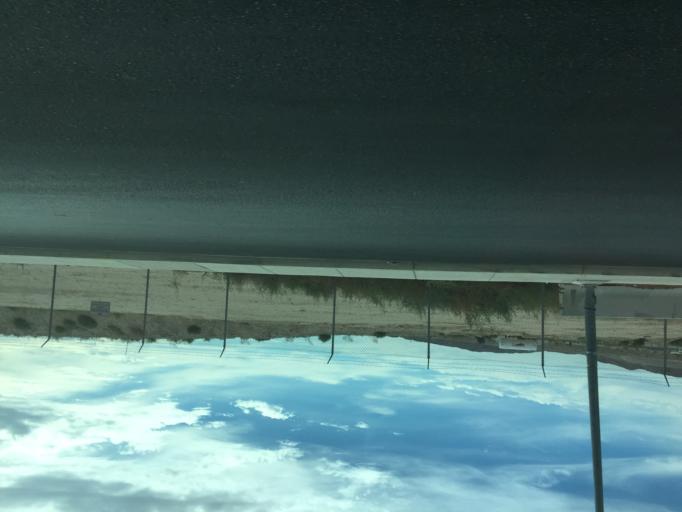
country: US
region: Nevada
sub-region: Clark County
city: Whitney
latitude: 36.1294
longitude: -115.0381
